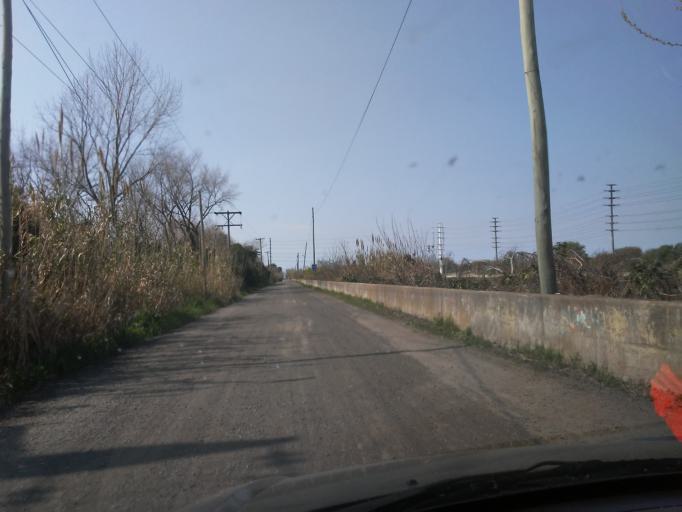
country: AR
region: Buenos Aires
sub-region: Partido de Avellaneda
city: Avellaneda
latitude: -34.6772
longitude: -58.3116
